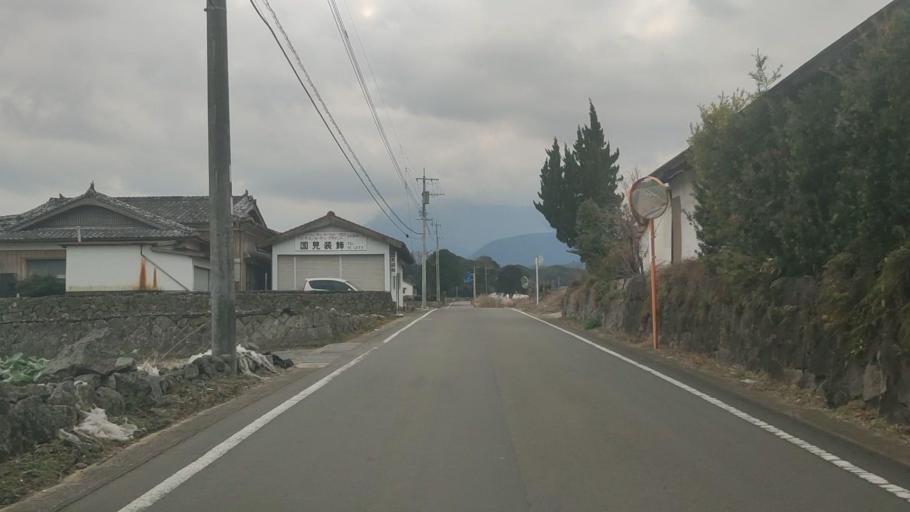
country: JP
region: Nagasaki
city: Shimabara
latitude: 32.8296
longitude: 130.2918
